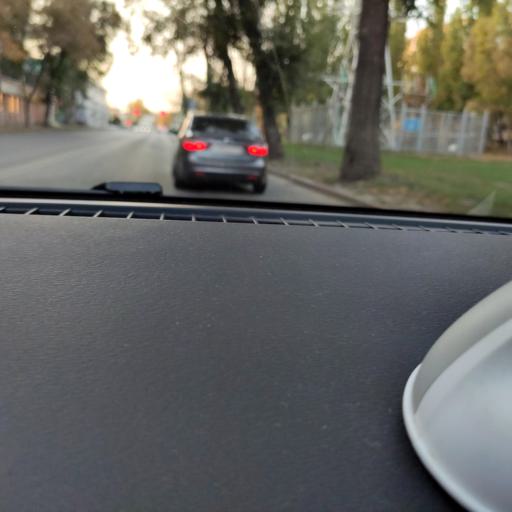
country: RU
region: Samara
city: Samara
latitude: 53.1963
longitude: 50.1361
